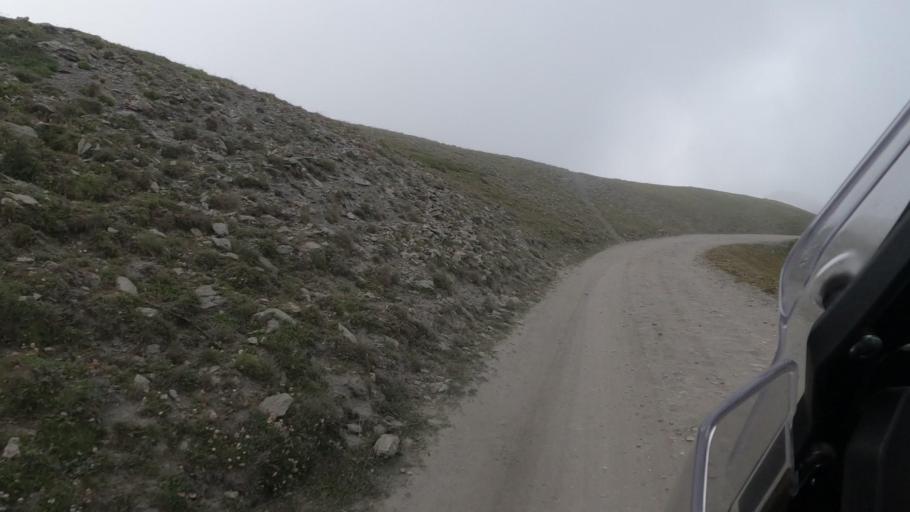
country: IT
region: Piedmont
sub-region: Provincia di Torino
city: Exilles
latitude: 45.0623
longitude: 6.9439
